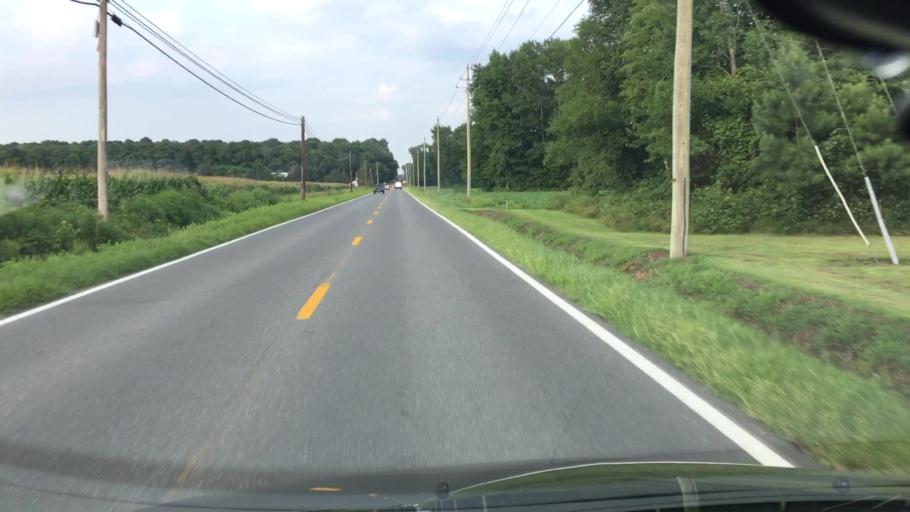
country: US
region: Delaware
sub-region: Sussex County
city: Selbyville
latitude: 38.4337
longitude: -75.2092
